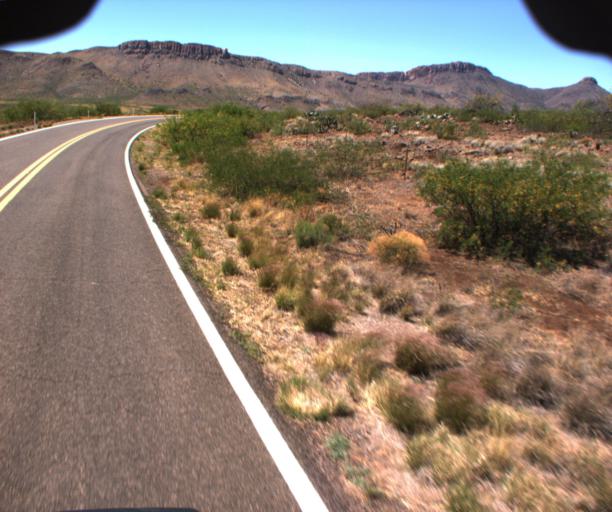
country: US
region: Arizona
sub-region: Cochise County
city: Douglas
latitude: 31.4615
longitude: -109.3662
